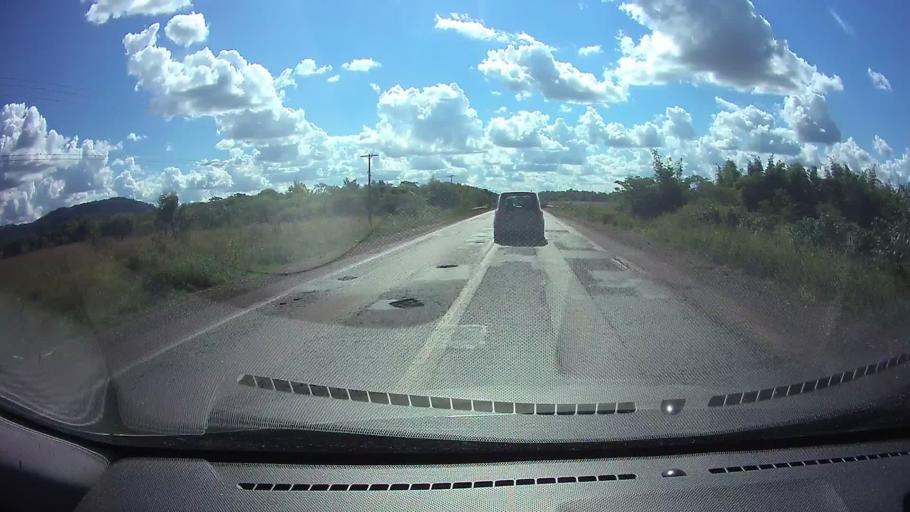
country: PY
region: Paraguari
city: La Colmena
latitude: -25.7529
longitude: -56.7792
